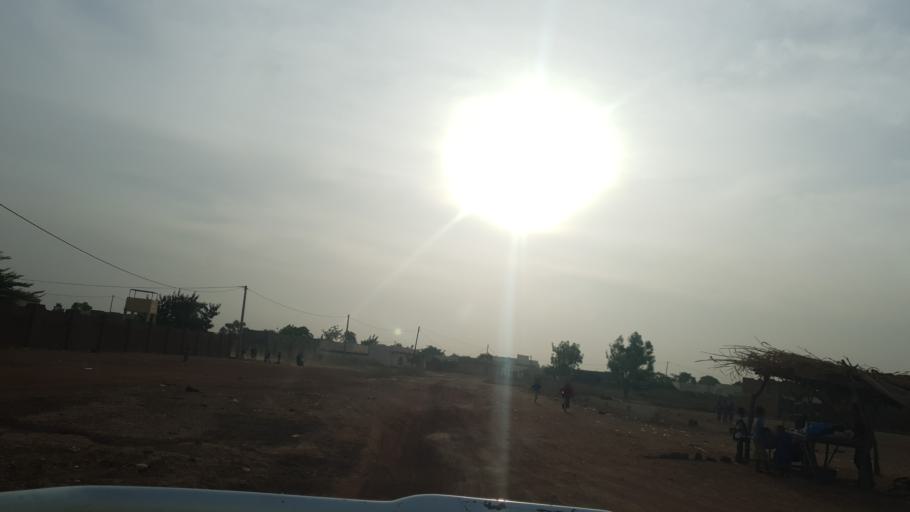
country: ML
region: Segou
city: Baroueli
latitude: 12.7744
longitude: -6.9382
